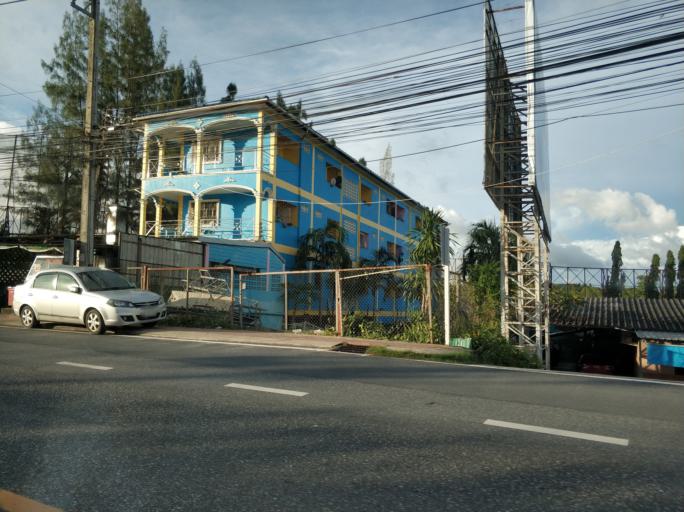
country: TH
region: Phuket
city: Kathu
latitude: 7.9020
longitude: 98.3398
